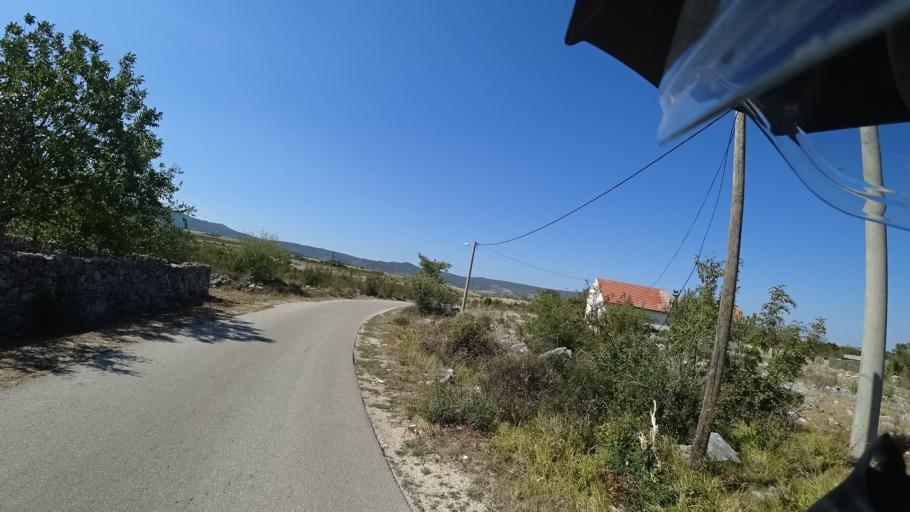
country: HR
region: Sibensko-Kniniska
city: Drnis
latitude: 43.8078
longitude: 16.3391
